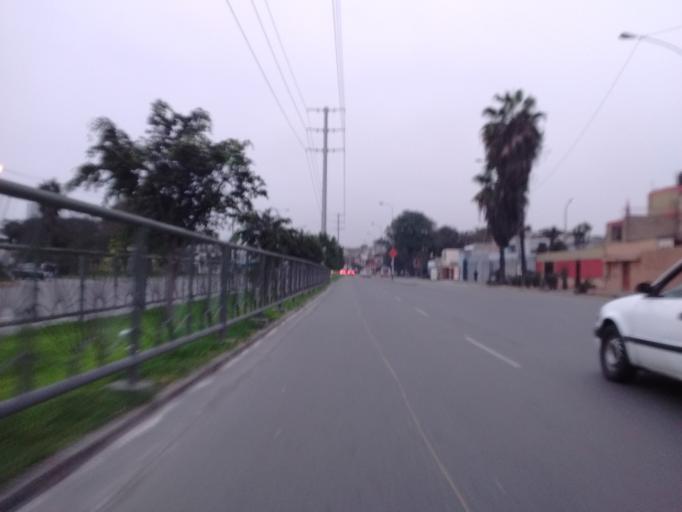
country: PE
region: Callao
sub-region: Callao
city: Callao
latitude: -12.0491
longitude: -77.0778
